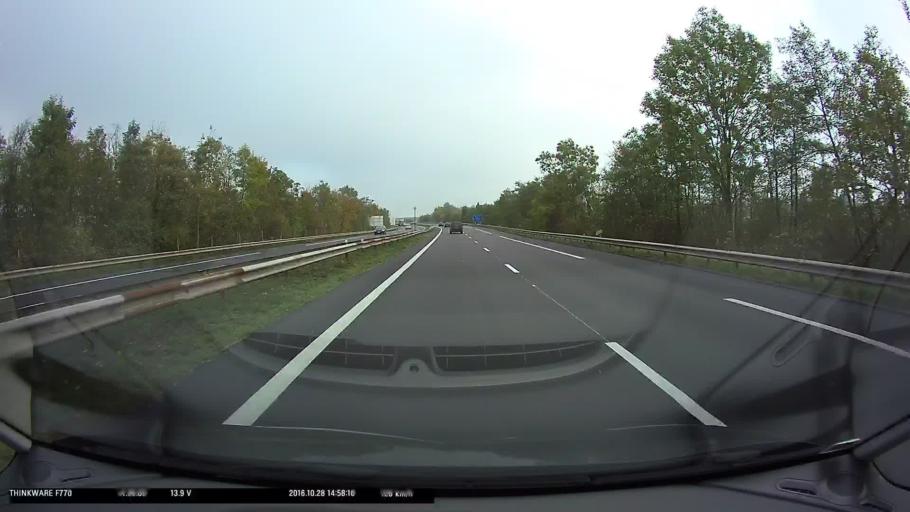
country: FR
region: Lorraine
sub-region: Departement de la Moselle
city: Phalsbourg
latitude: 48.7739
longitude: 7.2753
